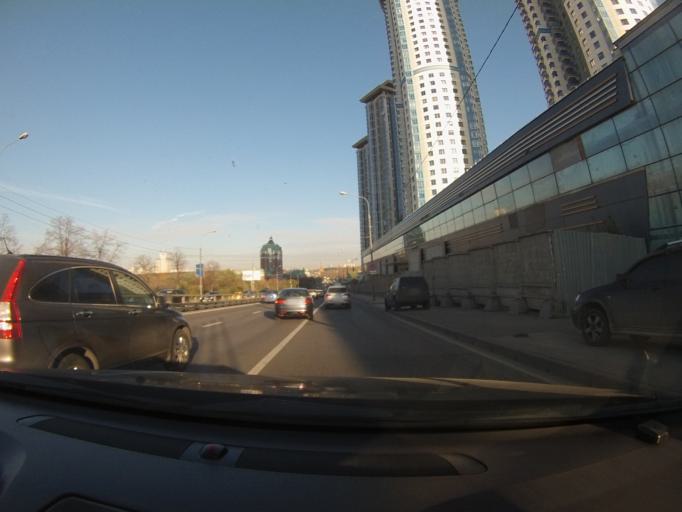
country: RU
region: Moskovskaya
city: Kastanayevo
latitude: 55.7136
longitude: 37.5045
